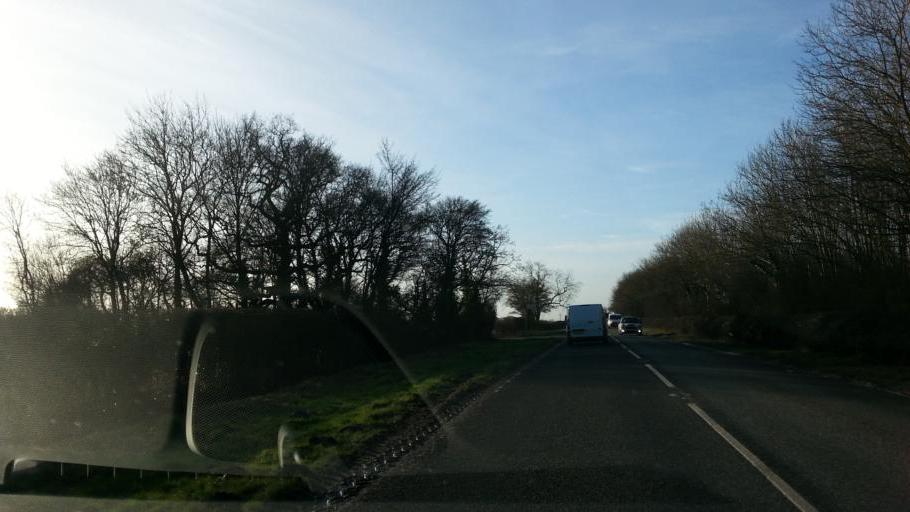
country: GB
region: England
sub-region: Lincolnshire
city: Grantham
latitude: 52.8755
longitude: -0.6002
